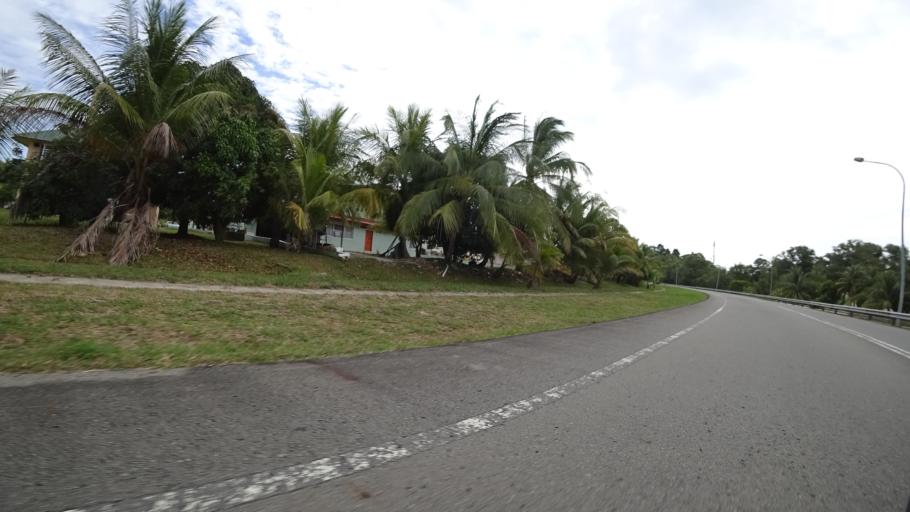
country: BN
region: Brunei and Muara
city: Bandar Seri Begawan
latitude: 4.9638
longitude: 114.9149
